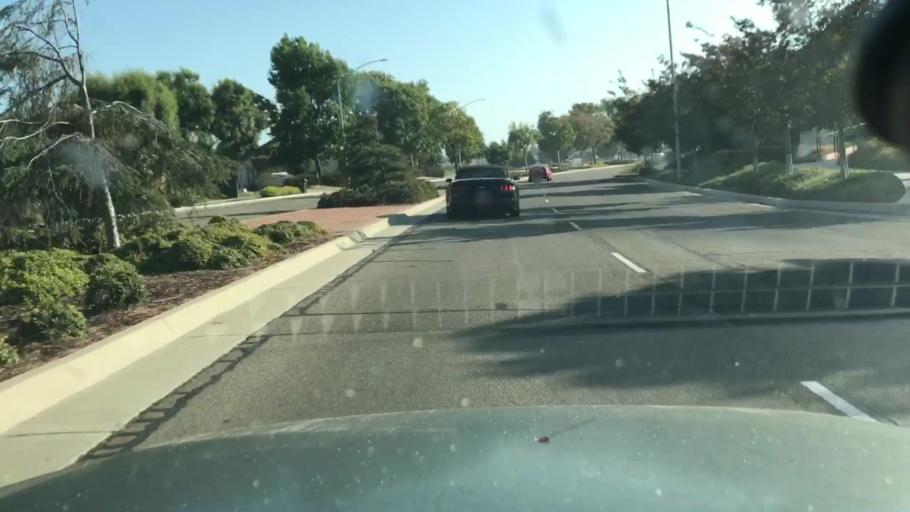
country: US
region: California
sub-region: Santa Barbara County
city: Santa Maria
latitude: 34.9119
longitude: -120.4318
